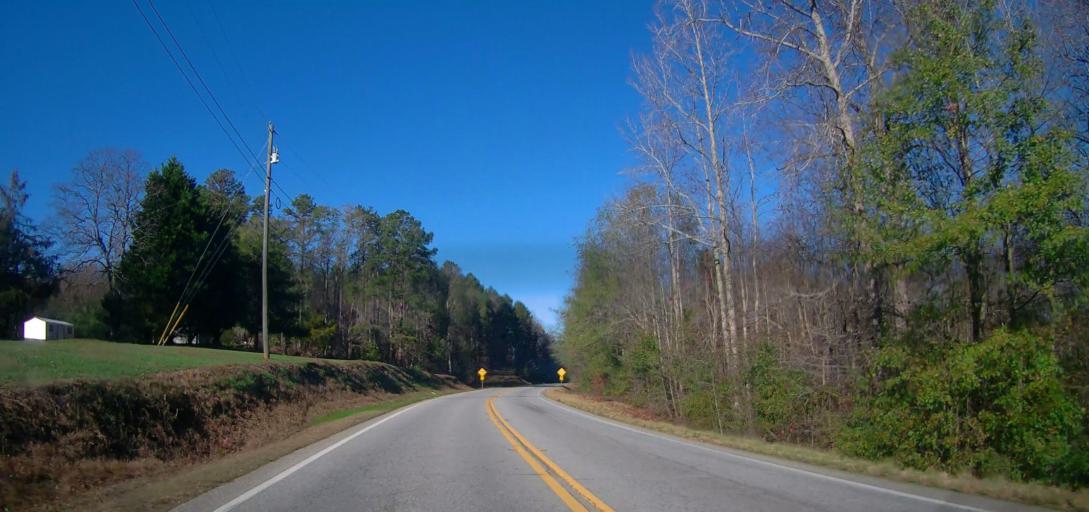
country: US
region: Georgia
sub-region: Hall County
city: Lula
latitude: 34.4096
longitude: -83.7100
